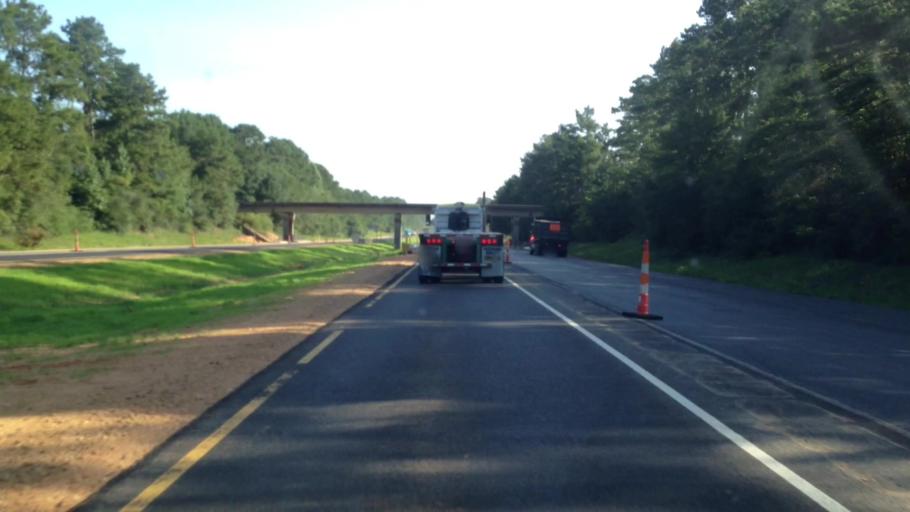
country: US
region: Mississippi
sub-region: Pike County
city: McComb
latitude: 31.2033
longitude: -90.4839
